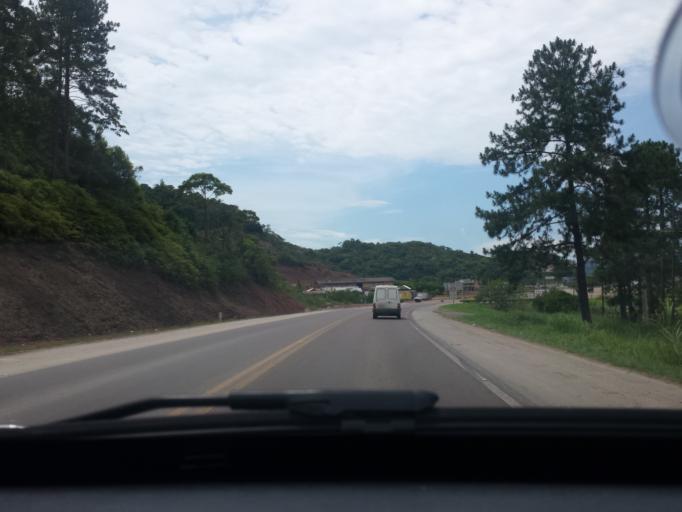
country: BR
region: Santa Catarina
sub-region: Gaspar
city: Gaspar
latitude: -26.9055
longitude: -48.9791
